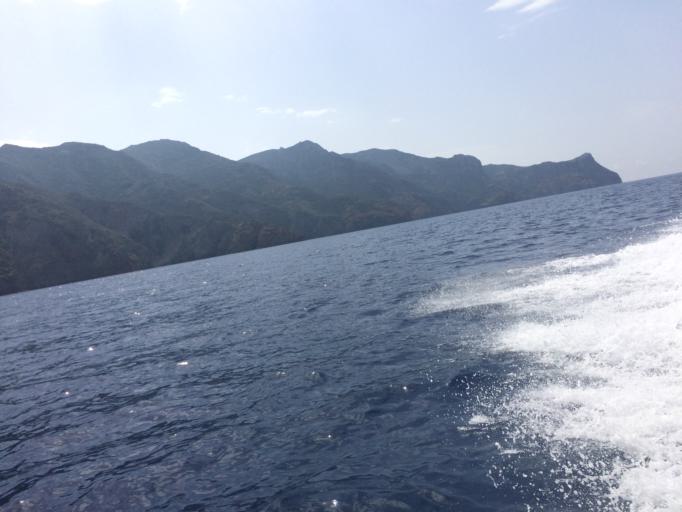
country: IT
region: Tuscany
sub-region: Provincia di Livorno
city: Capraia Isola
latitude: 43.0501
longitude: 9.7941
